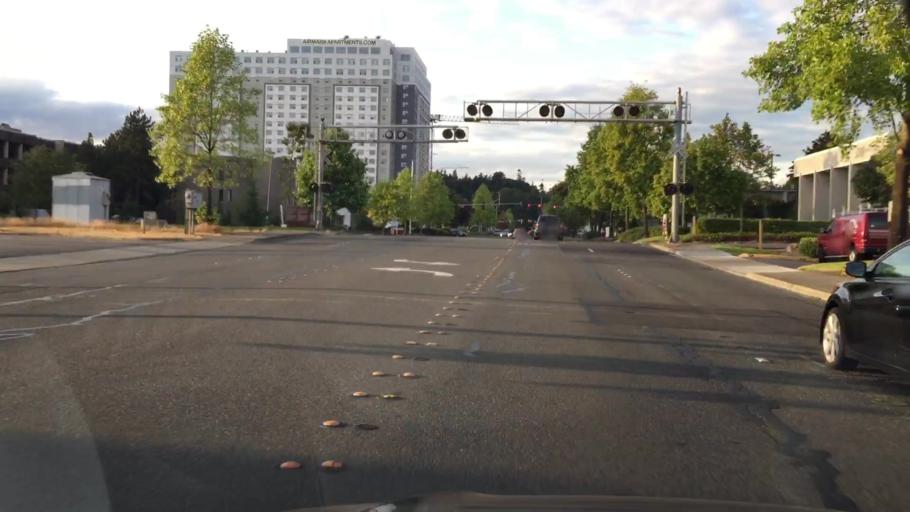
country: US
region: Washington
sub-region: King County
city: Tukwila
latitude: 47.4544
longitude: -122.2500
